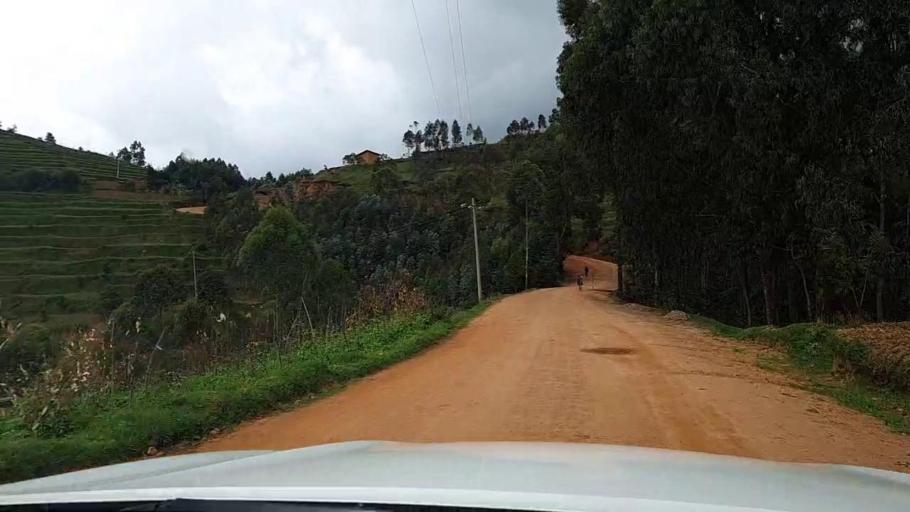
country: RW
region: Southern Province
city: Nzega
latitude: -2.4292
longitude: 29.4358
